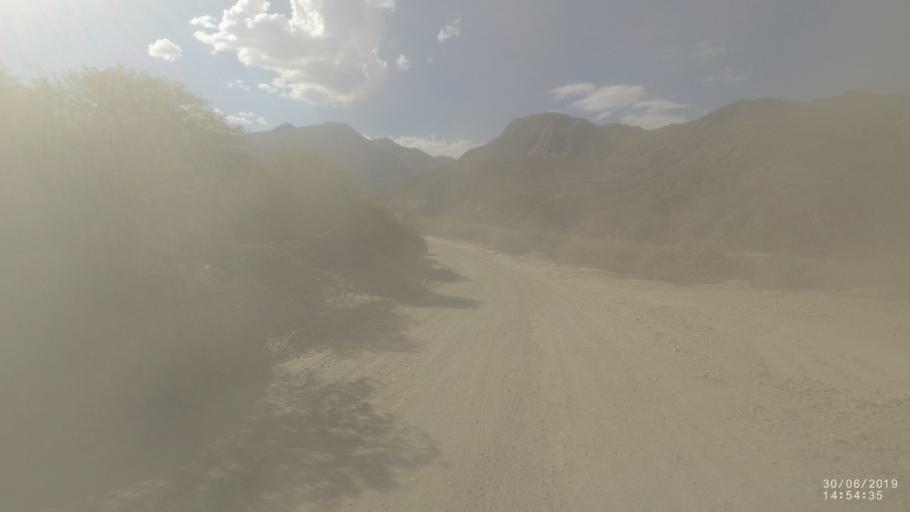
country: BO
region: Cochabamba
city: Irpa Irpa
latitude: -17.7579
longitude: -66.3504
